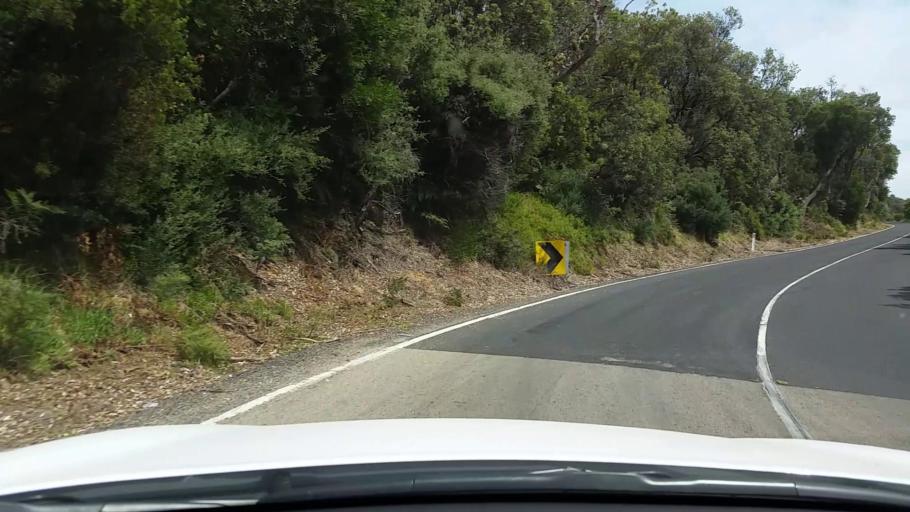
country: AU
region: Victoria
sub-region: Mornington Peninsula
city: Rosebud
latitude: -38.4771
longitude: 144.9324
